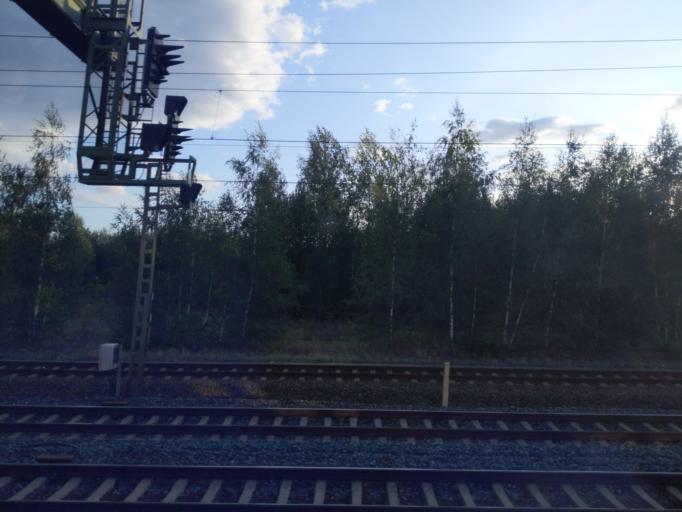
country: DE
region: Saxony
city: Heidenau
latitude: 50.9958
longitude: 13.8346
